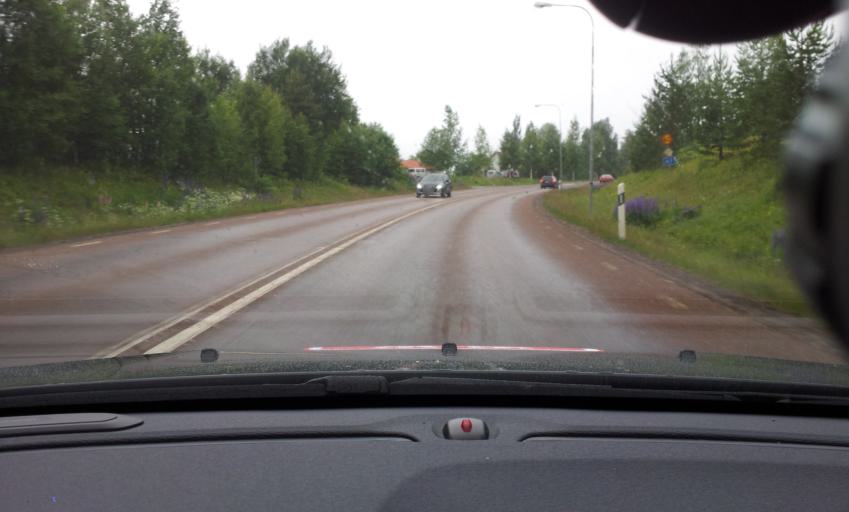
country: SE
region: Jaemtland
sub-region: Ragunda Kommun
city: Hammarstrand
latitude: 63.0116
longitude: 16.6587
